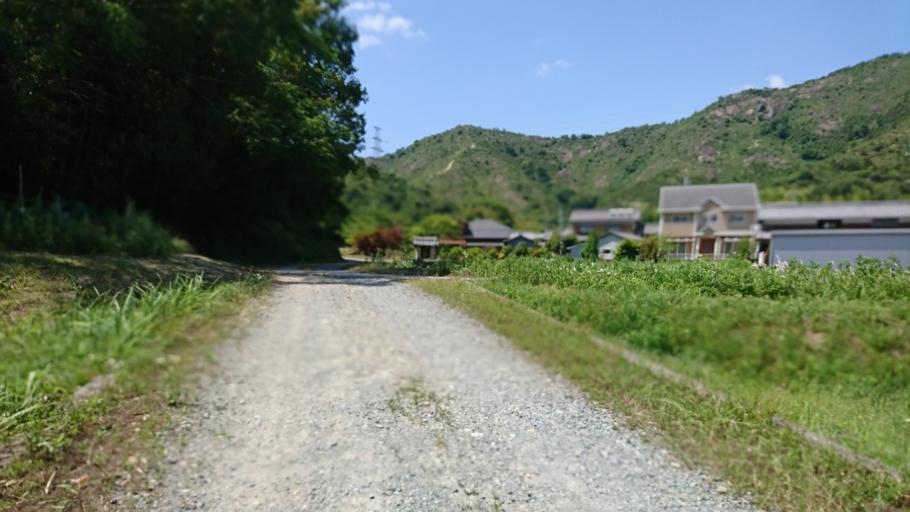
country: JP
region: Hyogo
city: Kakogawacho-honmachi
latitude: 34.8083
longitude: 134.7849
